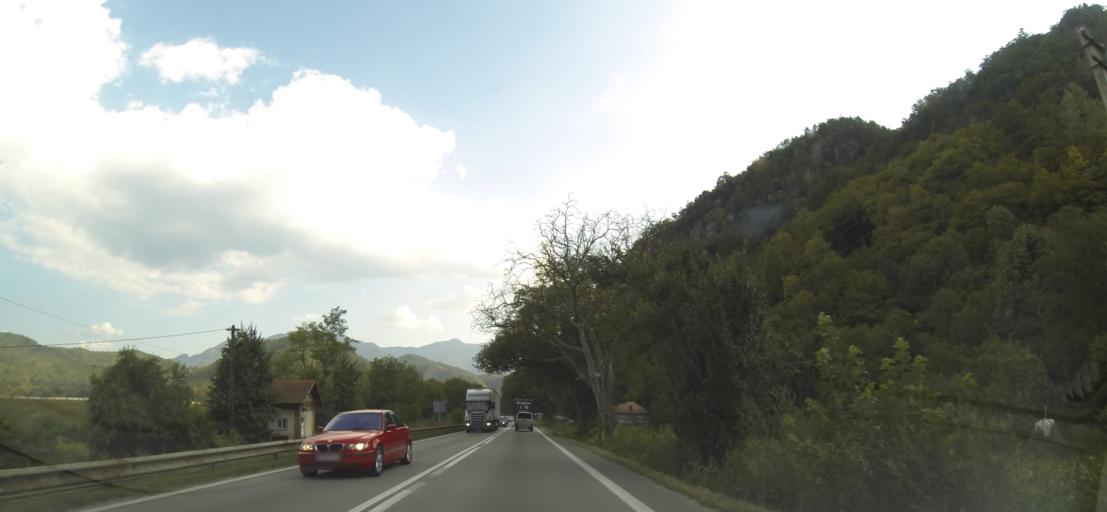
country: RO
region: Valcea
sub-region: Comuna Racovita
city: Racovita
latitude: 45.3959
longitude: 24.3009
